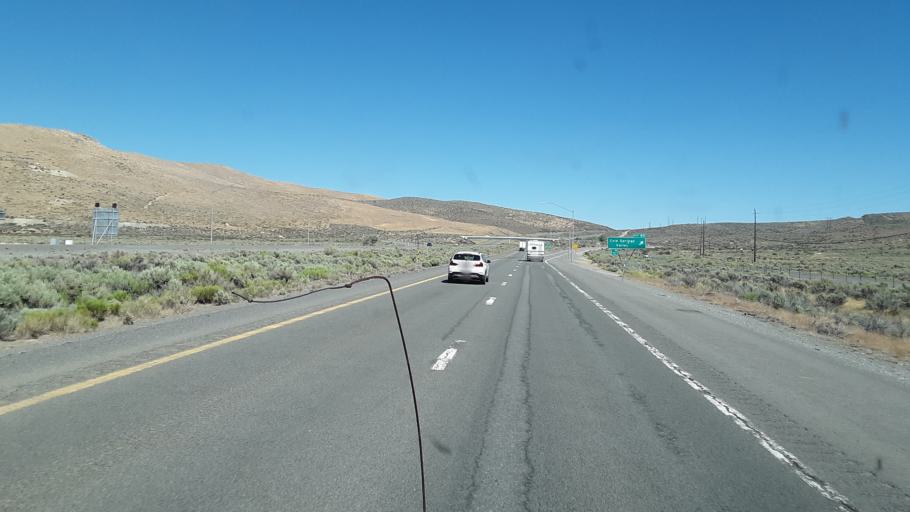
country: US
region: Nevada
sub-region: Washoe County
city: Cold Springs
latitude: 39.6463
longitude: -119.9658
